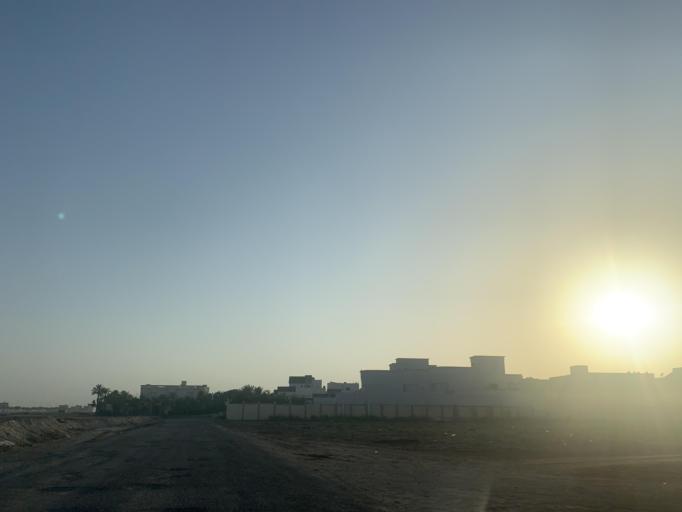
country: BH
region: Manama
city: Jidd Hafs
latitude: 26.1990
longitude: 50.5273
